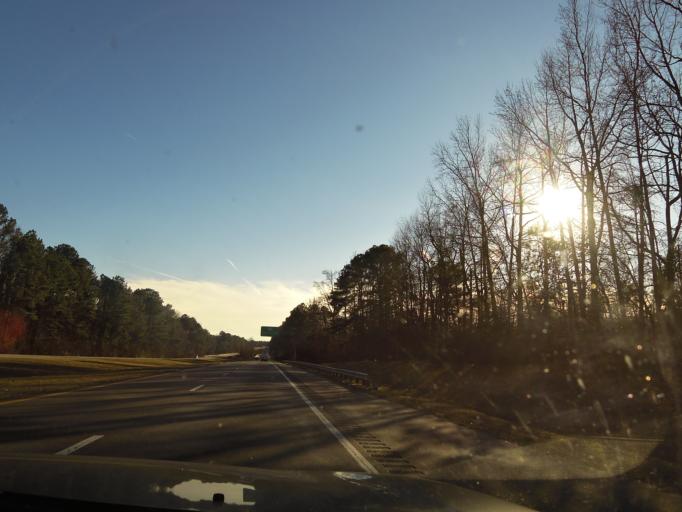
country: US
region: Virginia
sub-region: City of Suffolk
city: Suffolk
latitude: 36.7598
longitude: -76.6091
